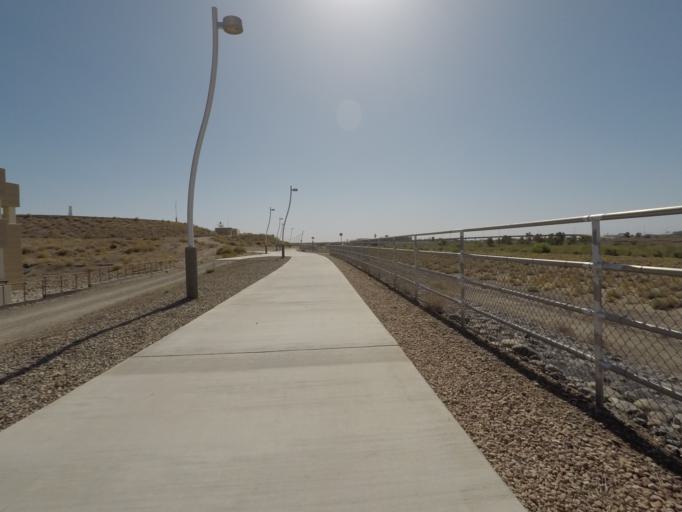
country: US
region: Arizona
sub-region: Maricopa County
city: Tempe Junction
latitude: 33.4342
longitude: -111.9687
